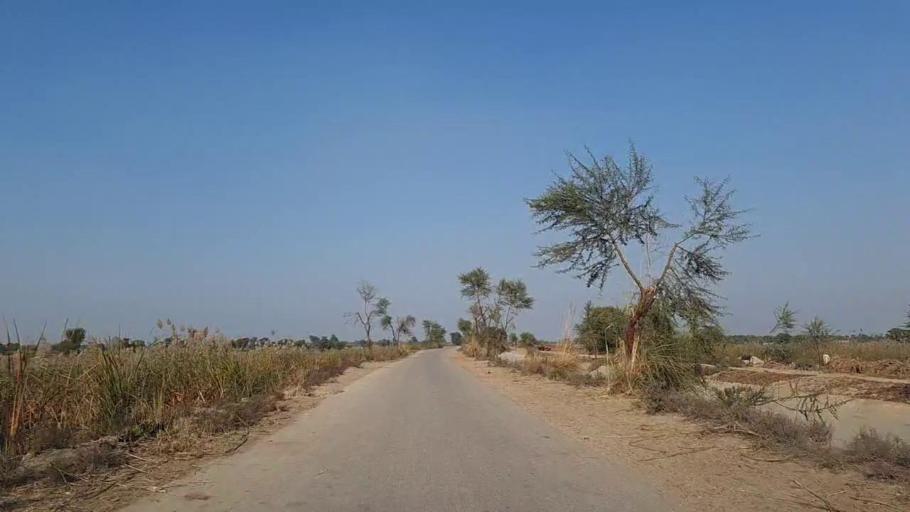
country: PK
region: Sindh
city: Daur
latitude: 26.4238
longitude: 68.2617
